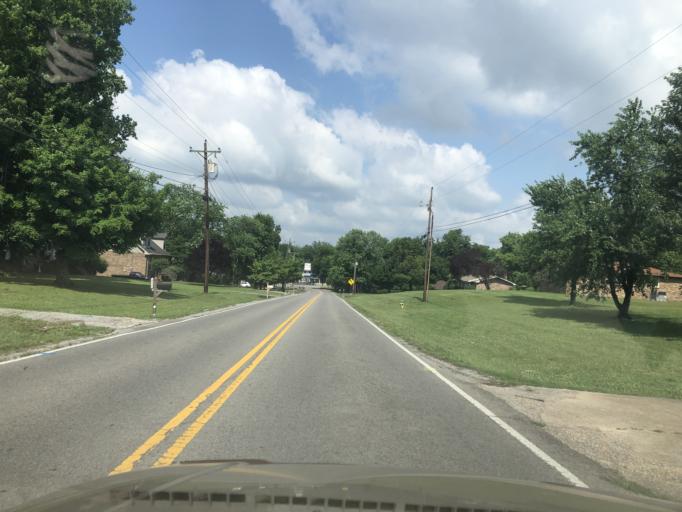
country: US
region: Tennessee
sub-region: Wilson County
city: Green Hill
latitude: 36.2303
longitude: -86.5856
